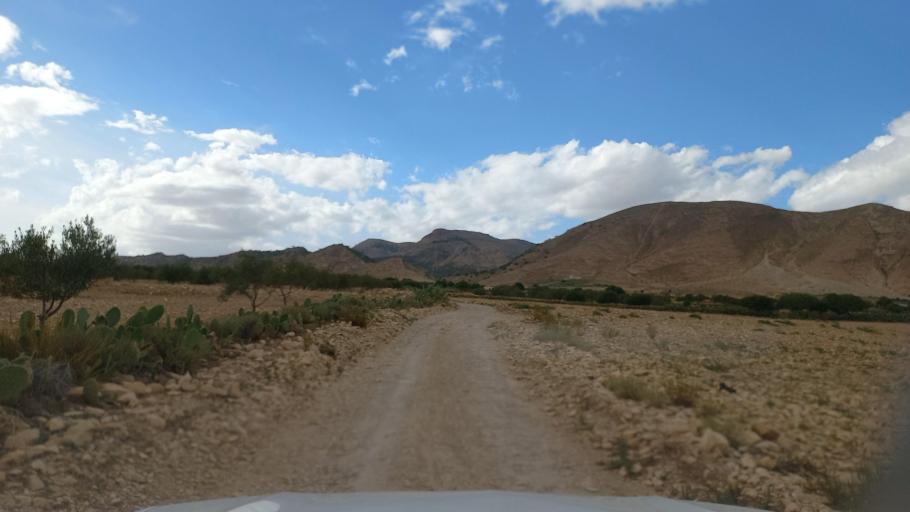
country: TN
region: Al Qasrayn
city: Sbiba
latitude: 35.4499
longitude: 9.0699
